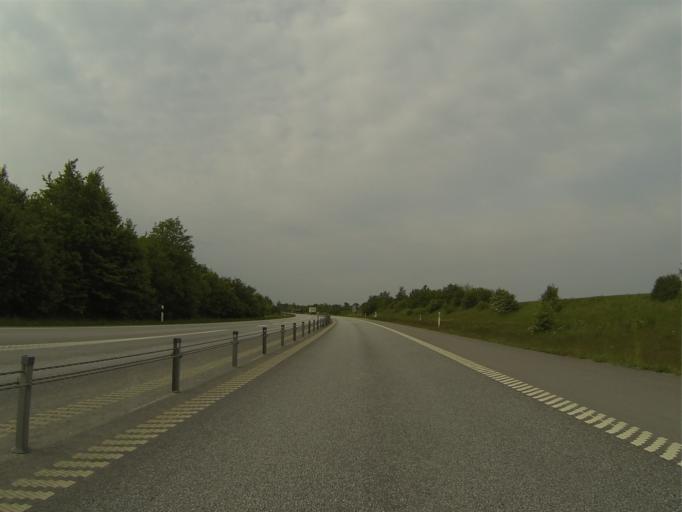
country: SE
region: Skane
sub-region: Staffanstorps Kommun
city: Staffanstorp
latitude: 55.6390
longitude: 13.2293
